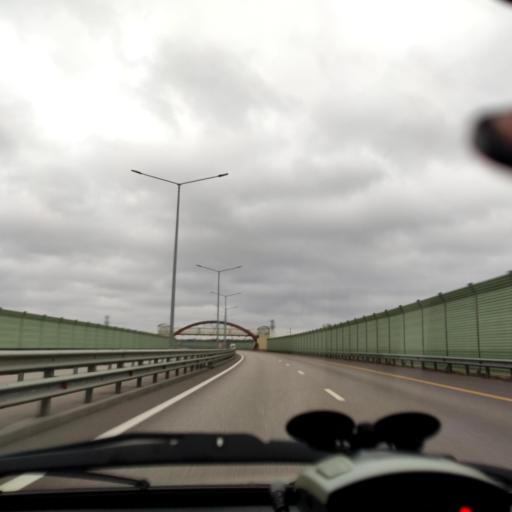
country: RU
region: Voronezj
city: Novaya Usman'
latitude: 51.6082
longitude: 39.3229
